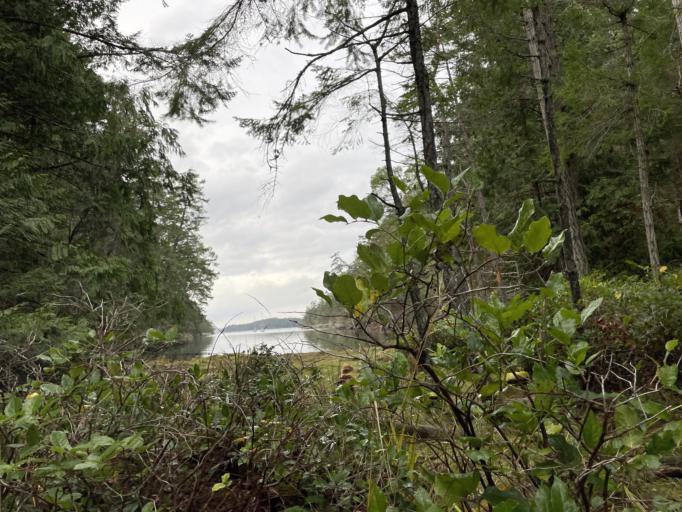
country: CA
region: British Columbia
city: North Cowichan
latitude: 48.9397
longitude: -123.5497
